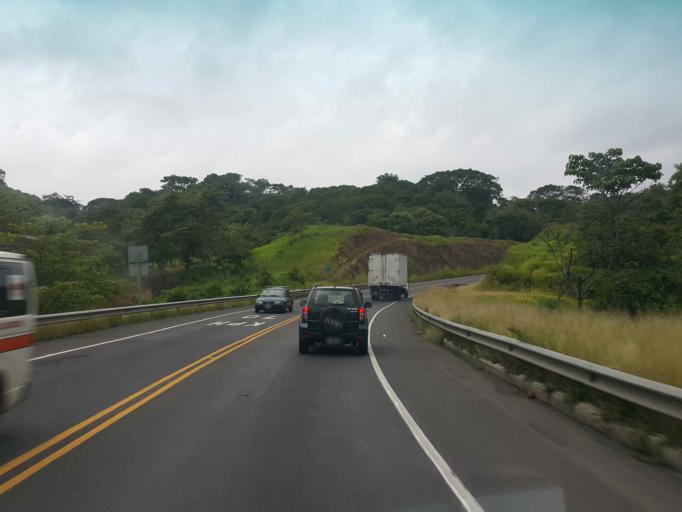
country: CR
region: Alajuela
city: Atenas
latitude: 9.9428
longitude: -84.3985
